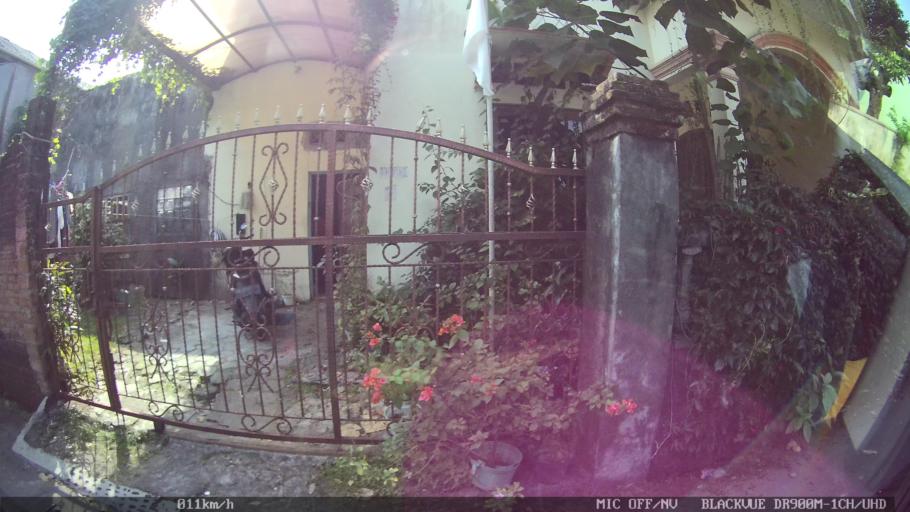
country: ID
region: Daerah Istimewa Yogyakarta
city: Yogyakarta
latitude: -7.8111
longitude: 110.3799
